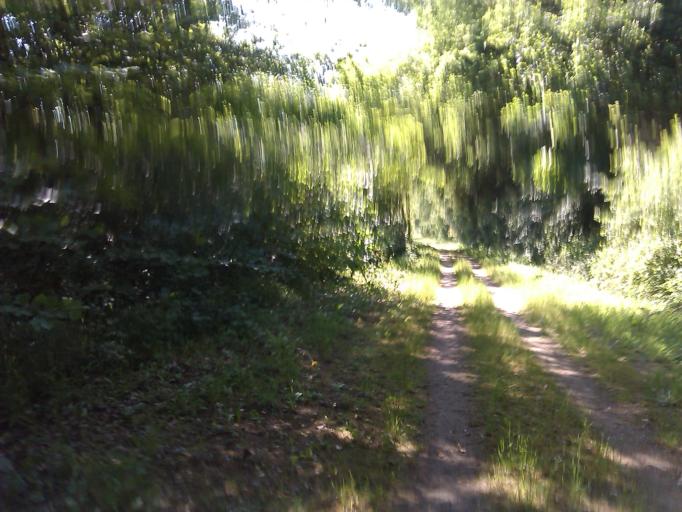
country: FR
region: Centre
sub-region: Departement de l'Indre
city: Belabre
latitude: 46.6298
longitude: 1.1871
